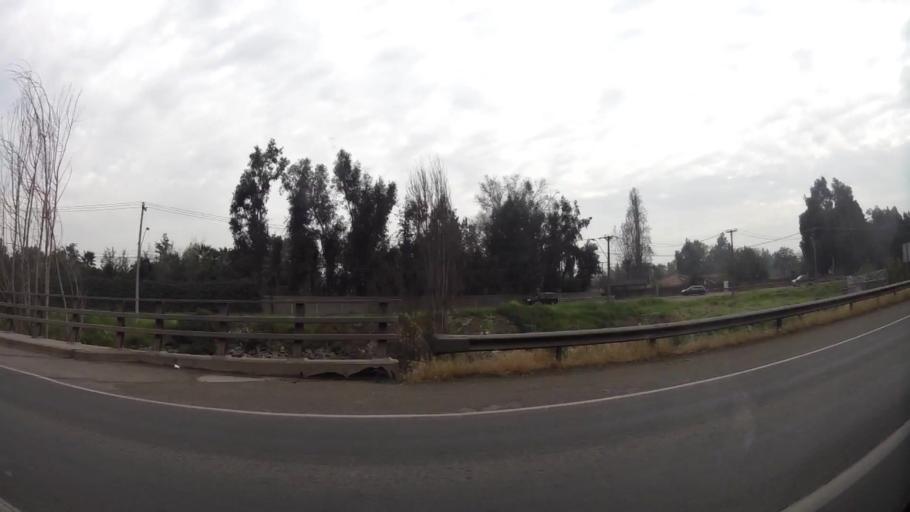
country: CL
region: Santiago Metropolitan
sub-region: Provincia de Chacabuco
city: Chicureo Abajo
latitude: -33.2423
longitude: -70.7033
